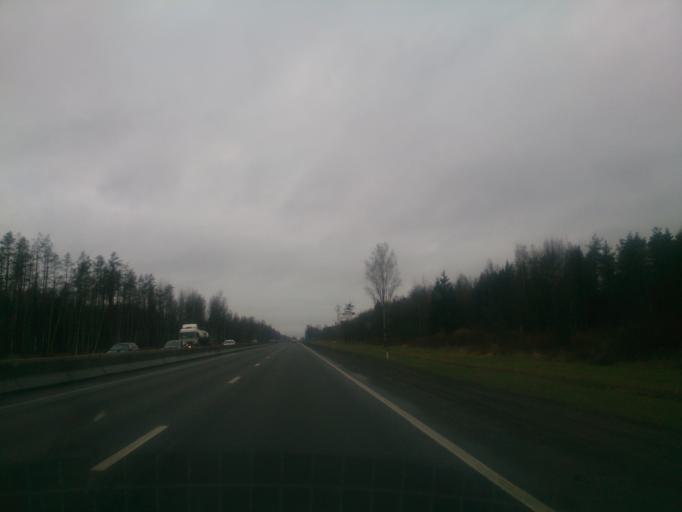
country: RU
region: Leningrad
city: Krasnyy Bor
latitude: 59.6359
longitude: 30.7039
